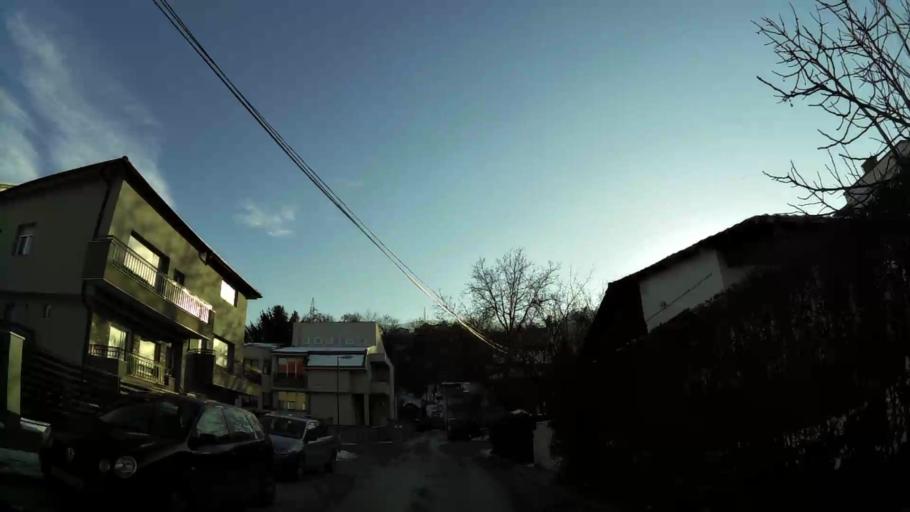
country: MK
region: Karpos
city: Skopje
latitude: 41.9923
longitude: 21.4026
